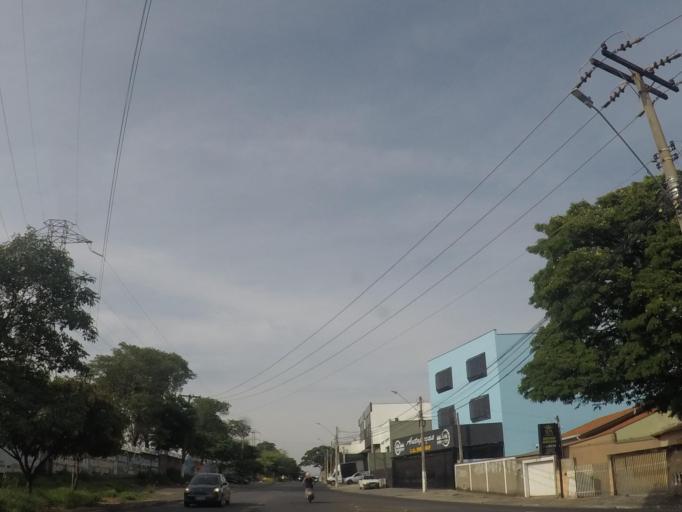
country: BR
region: Sao Paulo
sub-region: Hortolandia
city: Hortolandia
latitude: -22.8583
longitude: -47.1968
